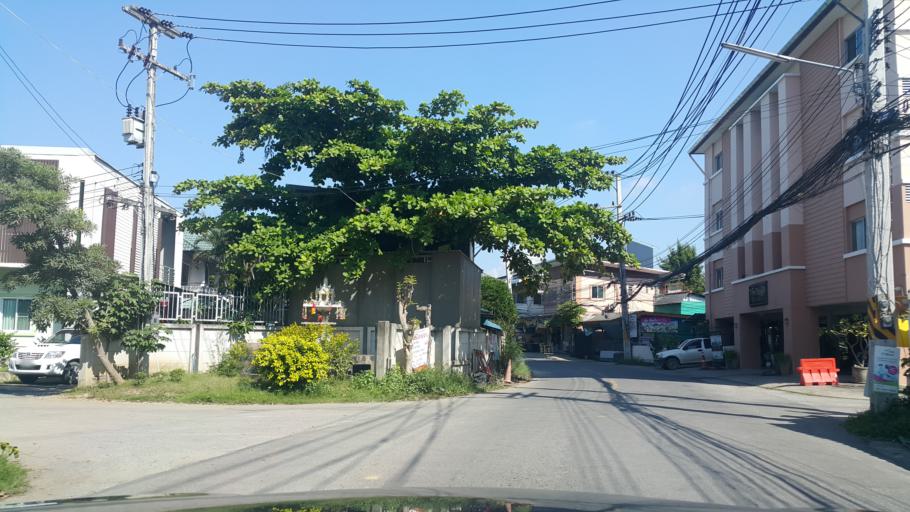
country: TH
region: Chiang Mai
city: Chiang Mai
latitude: 18.8066
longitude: 99.0127
